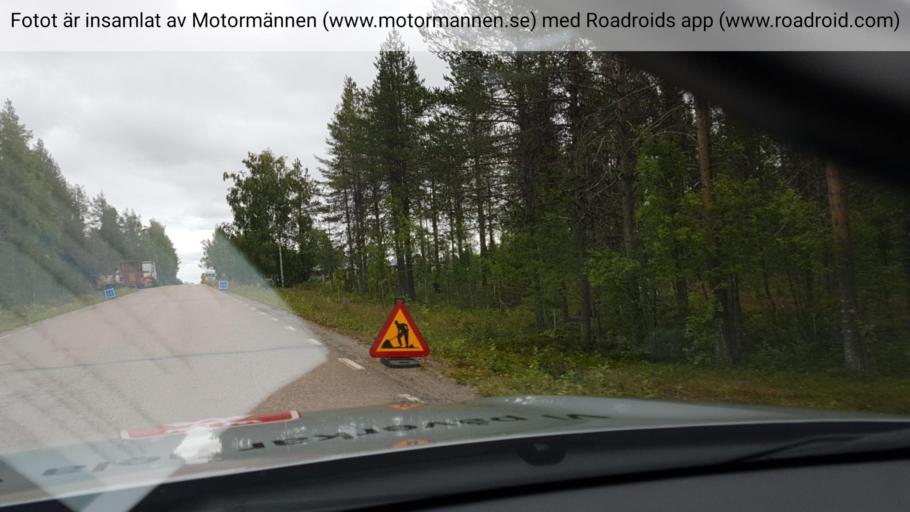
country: SE
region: Norrbotten
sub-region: Overkalix Kommun
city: OEverkalix
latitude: 67.0439
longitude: 22.0929
